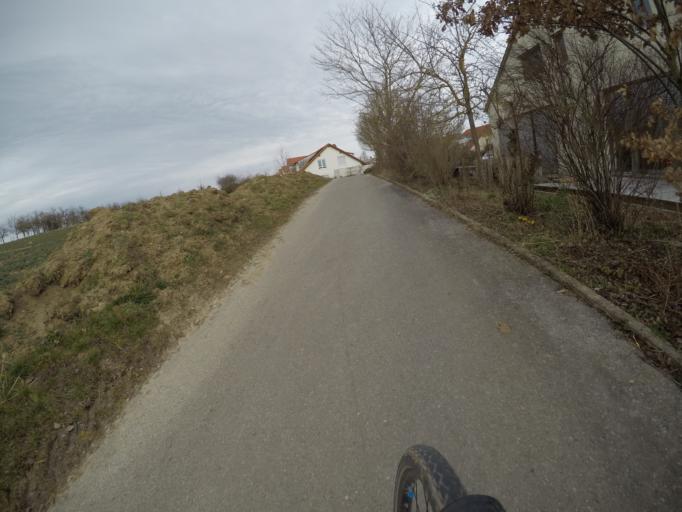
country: DE
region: Baden-Wuerttemberg
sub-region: Regierungsbezirk Stuttgart
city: Herrenberg
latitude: 48.5940
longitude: 8.8460
